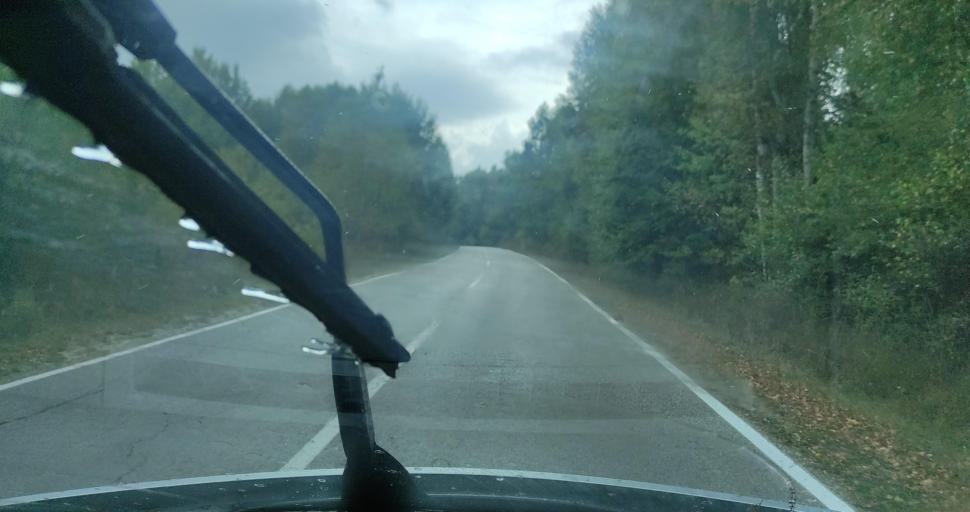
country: RS
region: Central Serbia
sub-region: Jablanicki Okrug
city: Crna Trava
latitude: 42.7162
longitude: 22.3295
